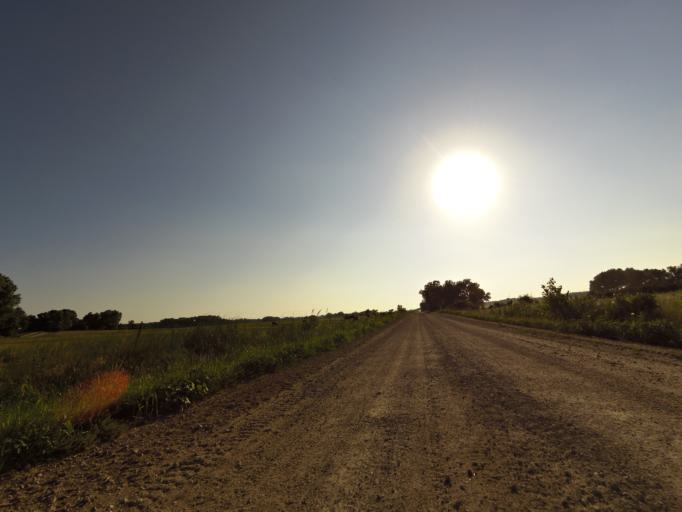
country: US
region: Kansas
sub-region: McPherson County
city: Inman
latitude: 38.1883
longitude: -97.8886
